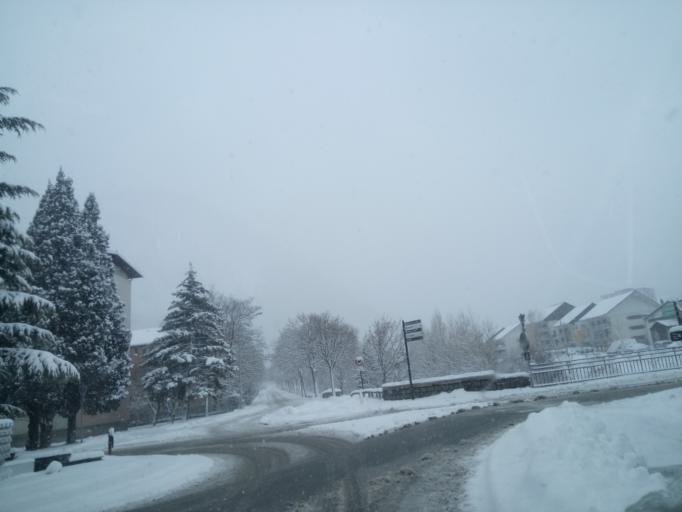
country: FR
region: Rhone-Alpes
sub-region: Departement de la Savoie
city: Saint-Jean-de-Maurienne
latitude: 45.2758
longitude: 6.3556
